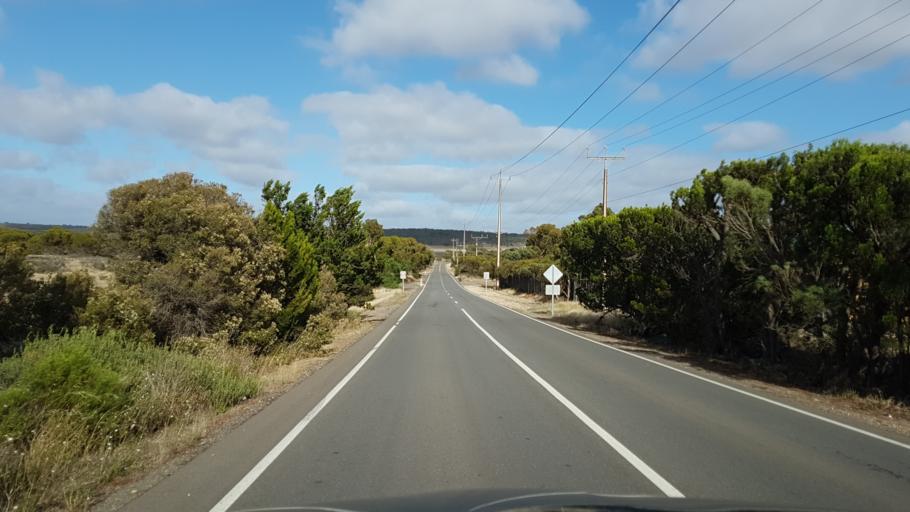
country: AU
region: South Australia
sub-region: Murray Bridge
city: Murray Bridge
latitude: -35.1168
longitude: 139.2455
